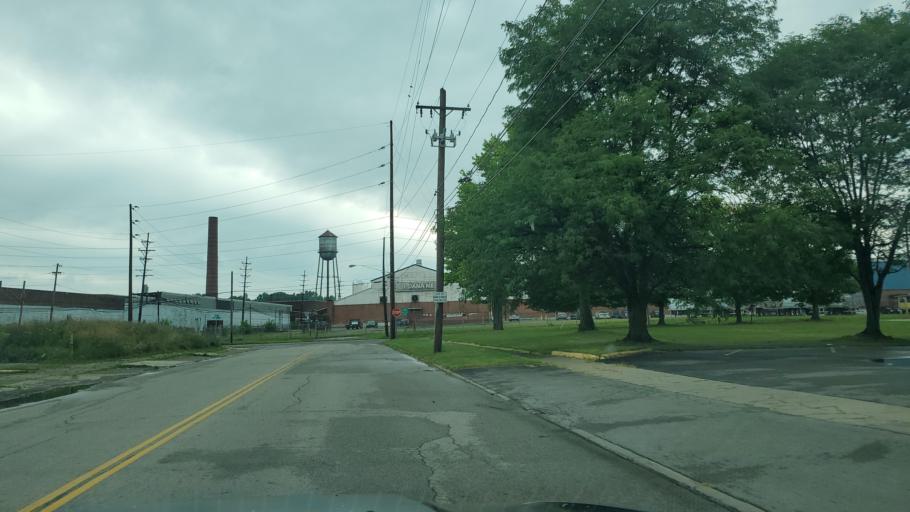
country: US
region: Ohio
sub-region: Trumbull County
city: Warren
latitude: 41.2473
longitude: -80.8100
